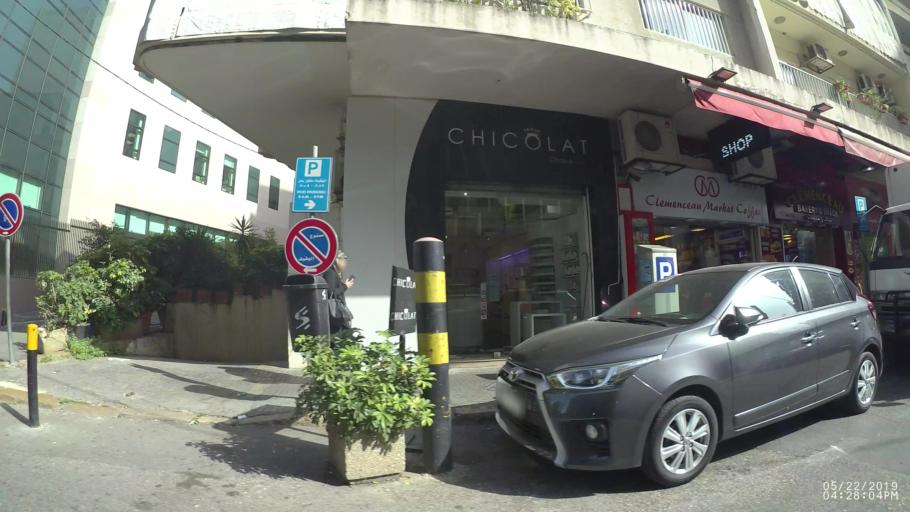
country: LB
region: Beyrouth
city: Ra's Bayrut
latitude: 33.8976
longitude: 35.4891
